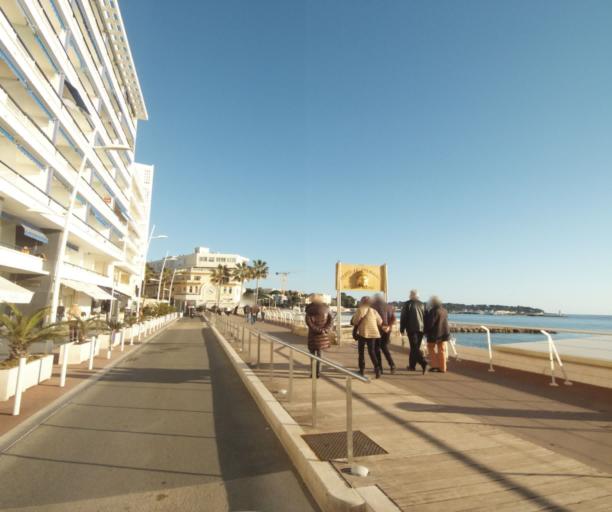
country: FR
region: Provence-Alpes-Cote d'Azur
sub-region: Departement des Alpes-Maritimes
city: Antibes
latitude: 43.5681
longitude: 7.1110
